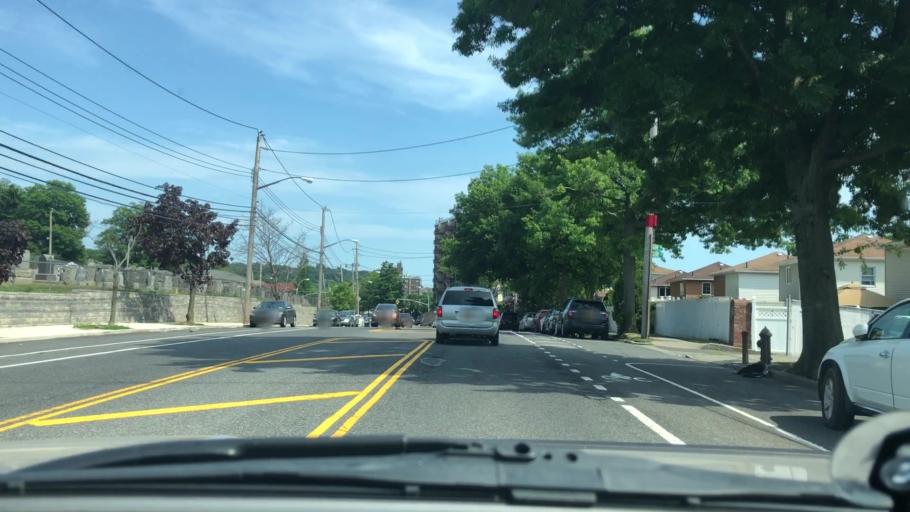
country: US
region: New Jersey
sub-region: Hudson County
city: Bayonne
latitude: 40.6218
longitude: -74.1118
